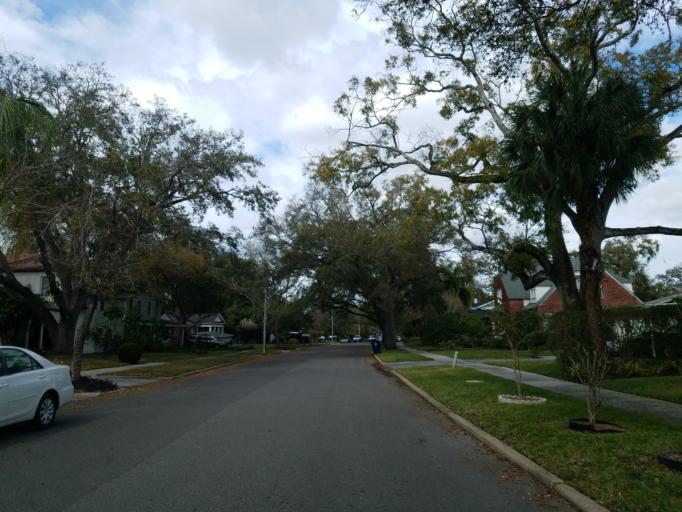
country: US
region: Florida
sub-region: Hillsborough County
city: Tampa
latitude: 27.9260
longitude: -82.4573
